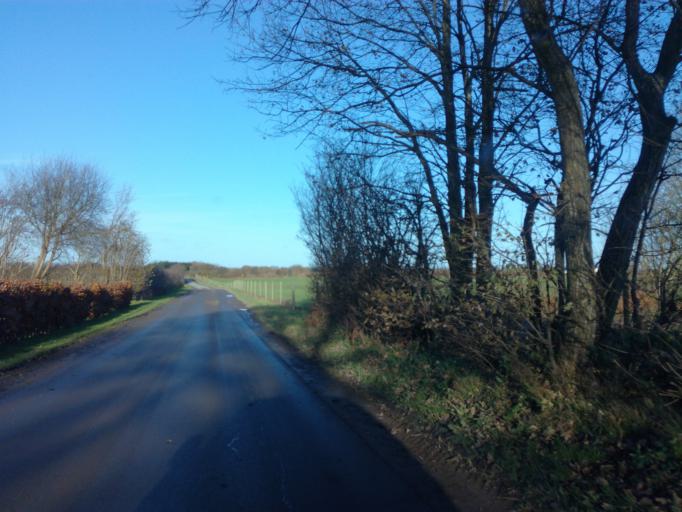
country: DK
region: South Denmark
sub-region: Vejle Kommune
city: Borkop
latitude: 55.6258
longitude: 9.6771
